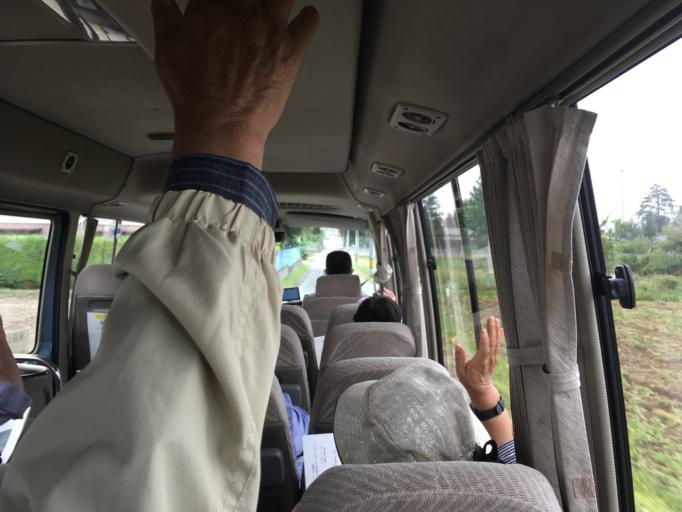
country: JP
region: Miyagi
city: Wakuya
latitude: 38.7259
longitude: 141.2585
